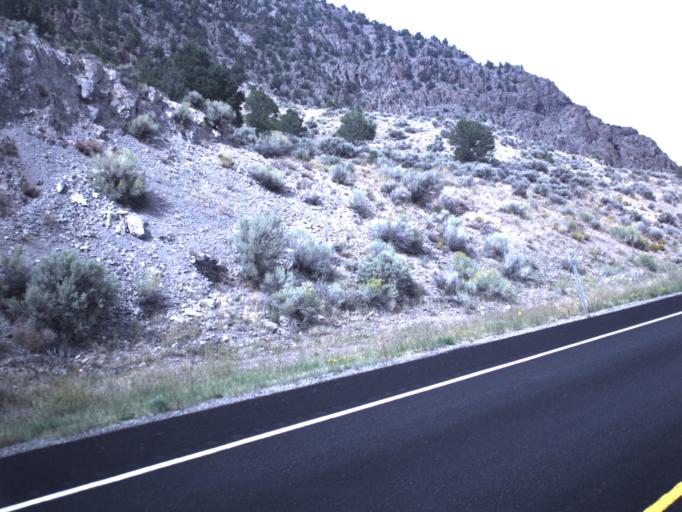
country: US
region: Utah
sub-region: Piute County
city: Junction
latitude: 38.0685
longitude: -112.3449
